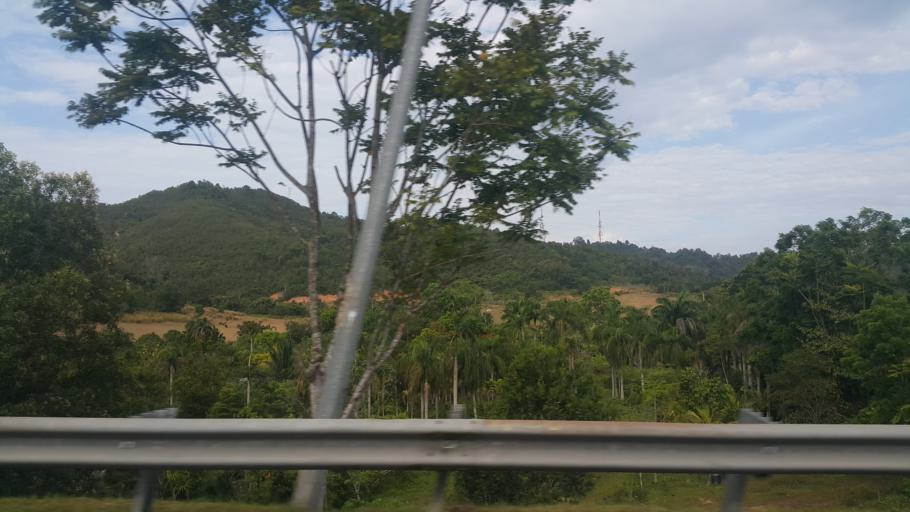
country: MY
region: Johor
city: Skudai
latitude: 1.4903
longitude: 103.6102
